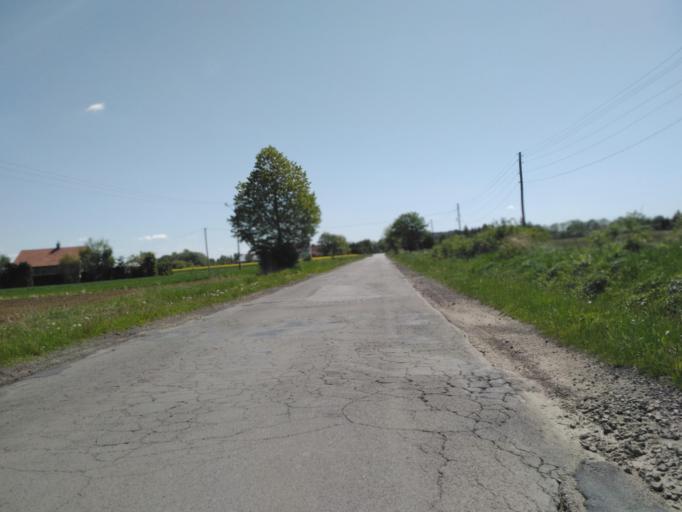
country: PL
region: Subcarpathian Voivodeship
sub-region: Powiat krosnienski
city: Miejsce Piastowe
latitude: 49.6058
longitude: 21.7846
